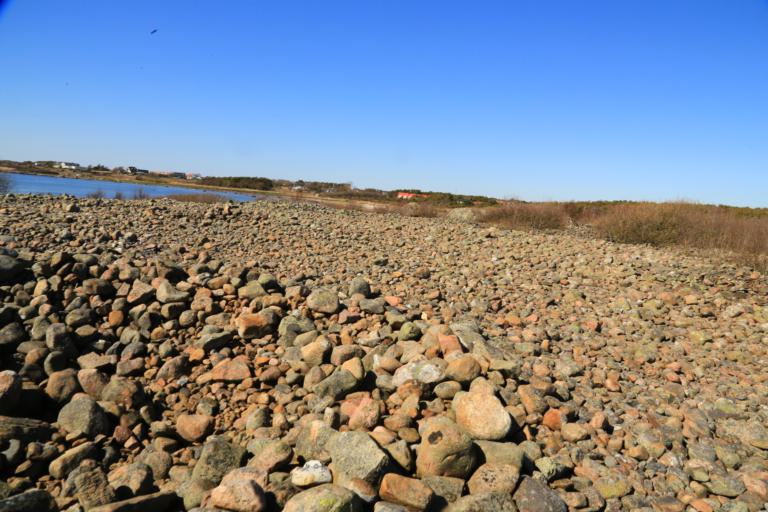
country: SE
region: Halland
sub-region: Varbergs Kommun
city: Traslovslage
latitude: 57.0446
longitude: 12.2867
